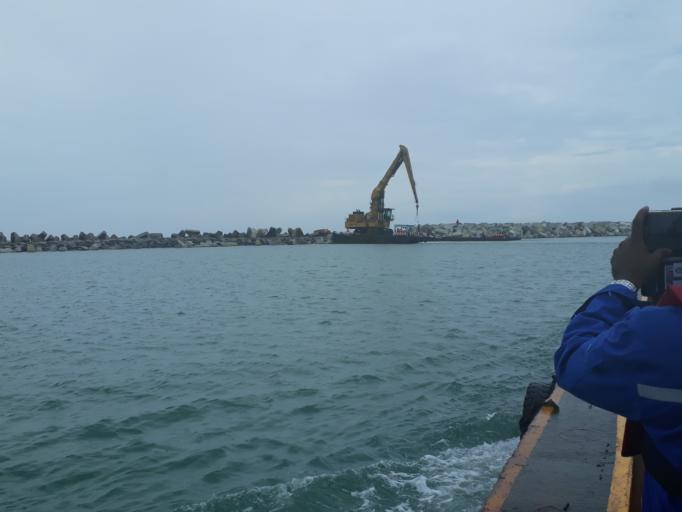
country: LK
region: Western
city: Colombo
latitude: 6.9241
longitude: 79.8282
